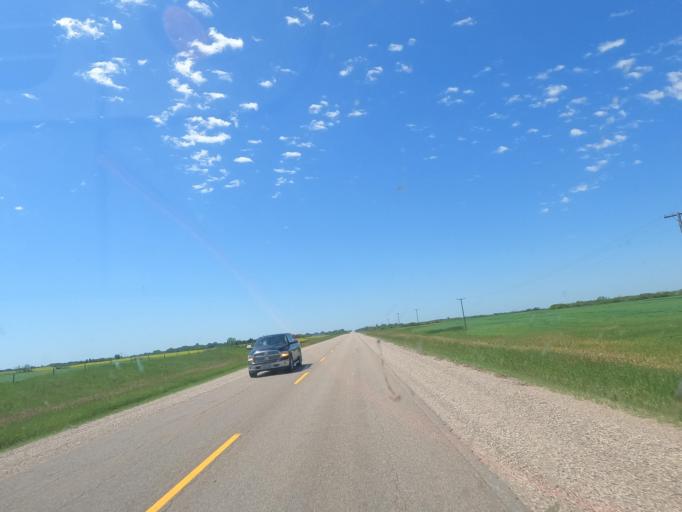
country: CA
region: Manitoba
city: Melita
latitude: 49.5624
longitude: -101.0621
